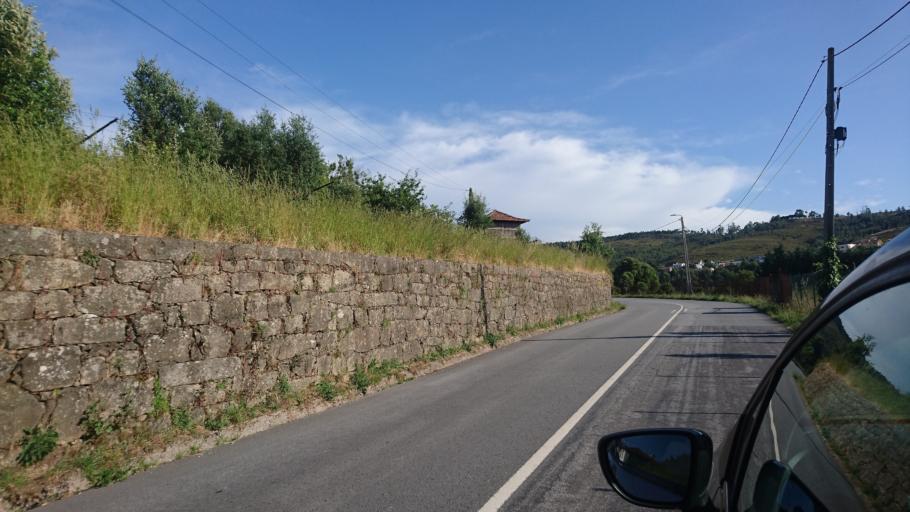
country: PT
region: Porto
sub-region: Paredes
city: Recarei
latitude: 41.1404
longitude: -8.3880
